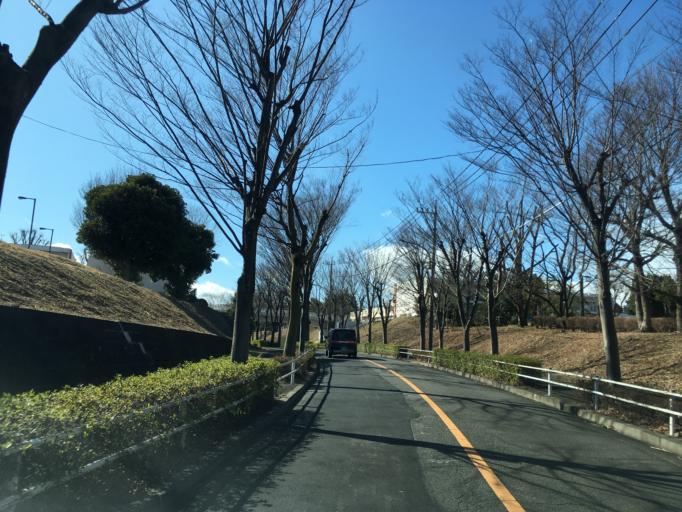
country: JP
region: Tokyo
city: Hino
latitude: 35.6161
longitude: 139.4314
